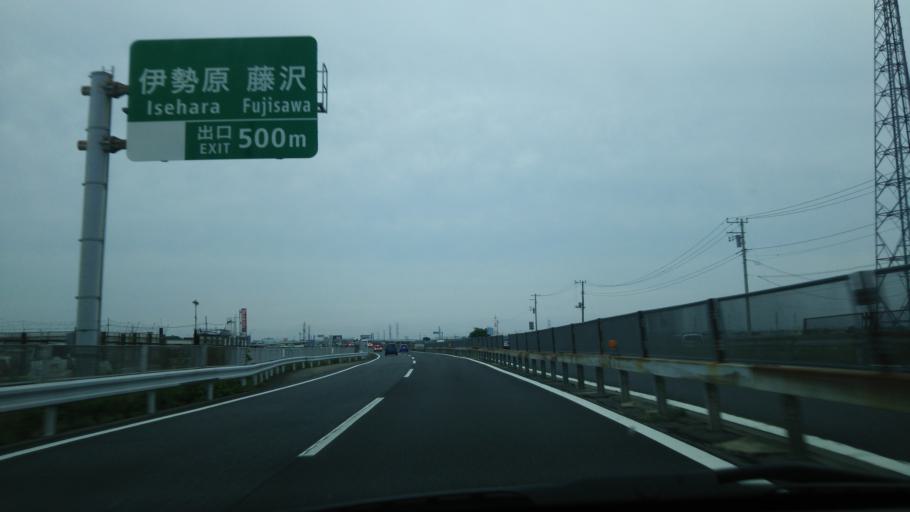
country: JP
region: Kanagawa
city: Isehara
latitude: 35.3788
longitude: 139.3283
